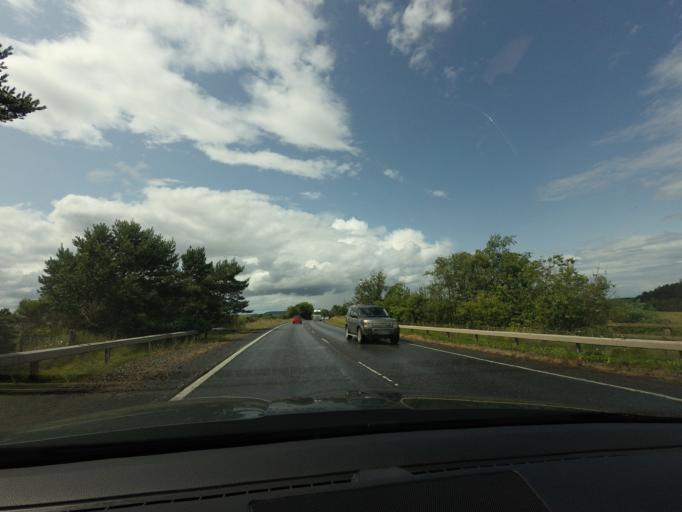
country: GB
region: Scotland
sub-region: Moray
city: Lhanbryd
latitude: 57.6341
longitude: -3.2280
